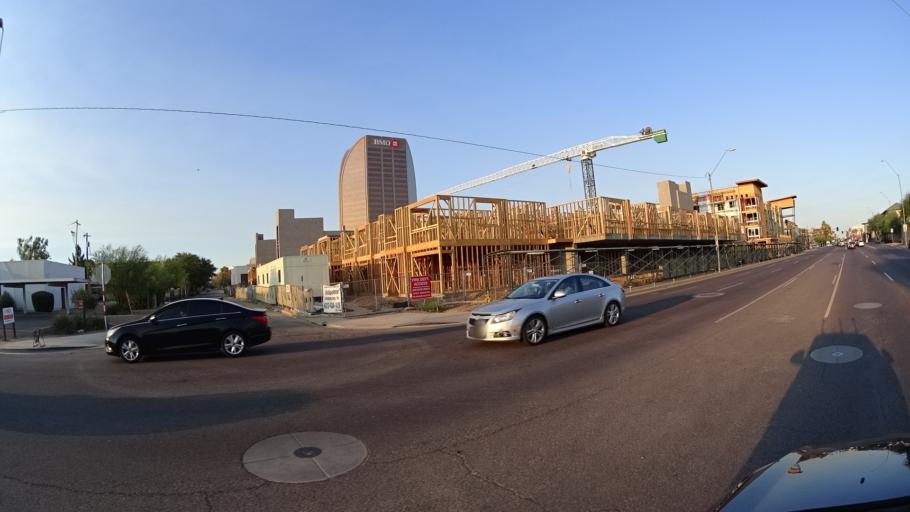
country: US
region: Arizona
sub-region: Maricopa County
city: Phoenix
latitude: 33.4657
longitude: -112.0760
